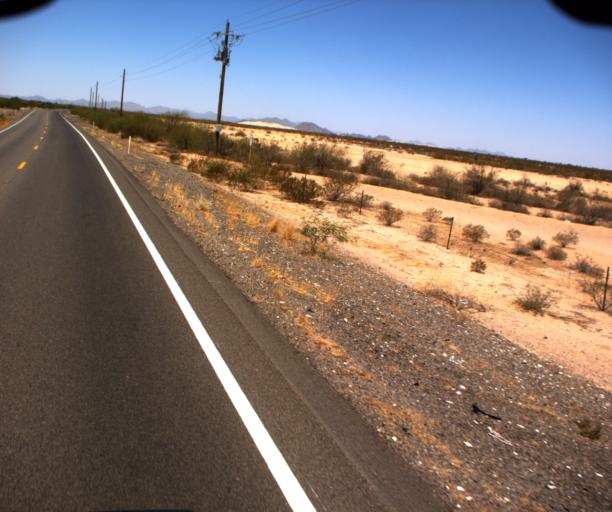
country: US
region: Arizona
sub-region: Pinal County
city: Maricopa
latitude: 33.0718
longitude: -112.2036
